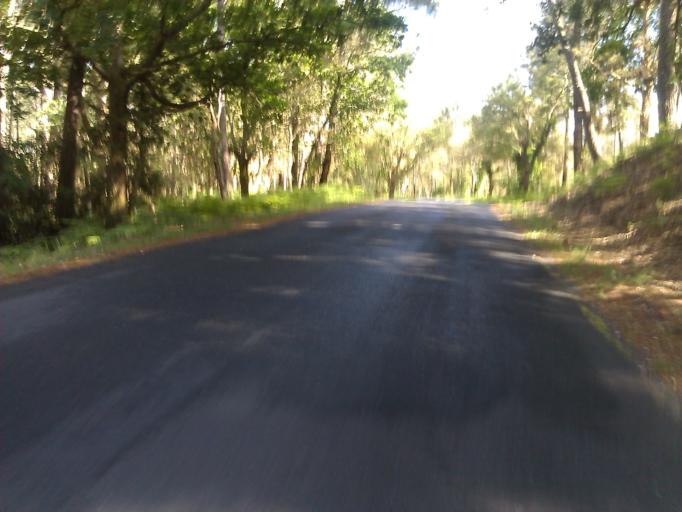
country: FR
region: Aquitaine
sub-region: Departement des Landes
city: Leon
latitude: 43.8661
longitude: -1.3602
